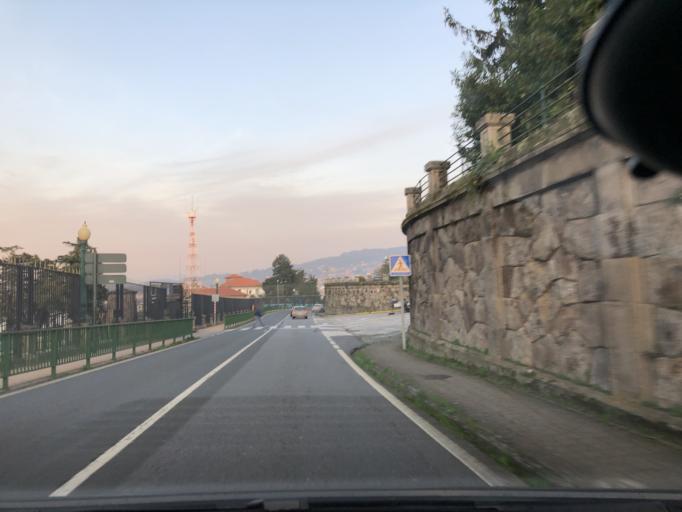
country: ES
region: Galicia
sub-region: Provincia de Pontevedra
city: Marin
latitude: 42.3939
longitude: -8.7090
